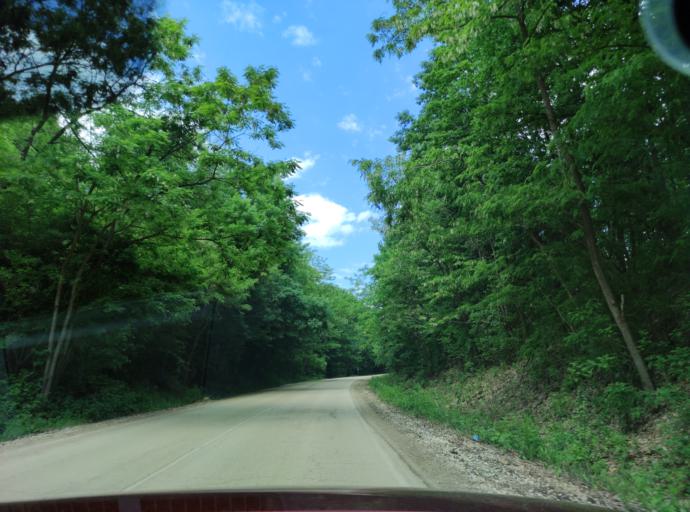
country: BG
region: Montana
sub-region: Obshtina Berkovitsa
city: Berkovitsa
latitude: 43.3775
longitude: 23.0761
